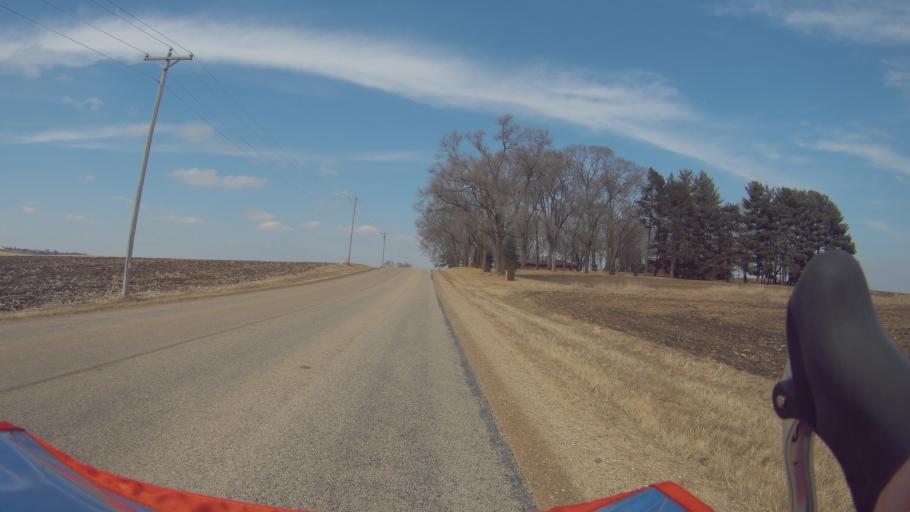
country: US
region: Wisconsin
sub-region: Dane County
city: Waunakee
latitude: 43.1651
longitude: -89.4967
